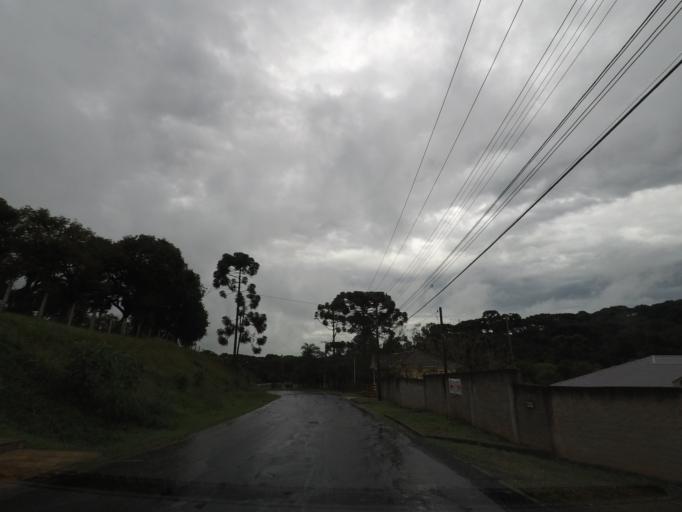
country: BR
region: Parana
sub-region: Campo Largo
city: Campo Largo
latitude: -25.4495
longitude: -49.4427
